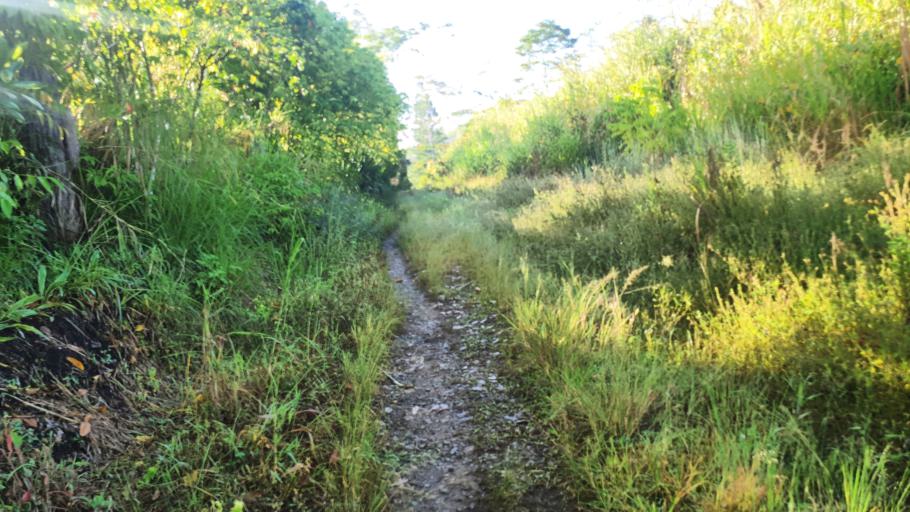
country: PG
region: Western Highlands
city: Rauna
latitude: -5.8005
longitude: 144.3660
